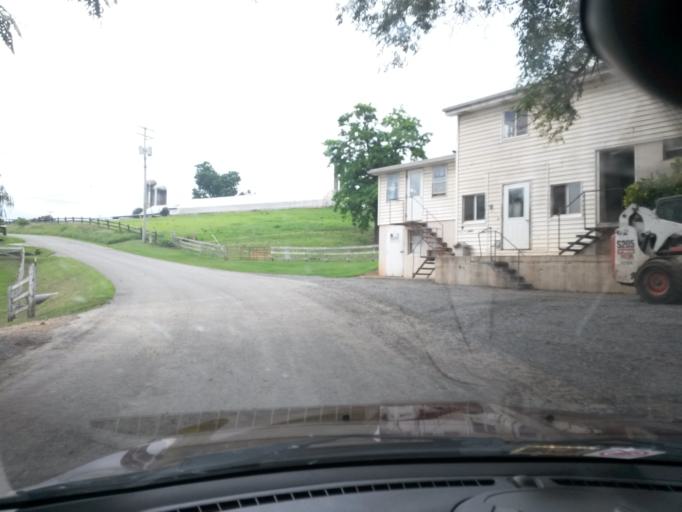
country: US
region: Virginia
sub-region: Rockingham County
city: Dayton
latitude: 38.4426
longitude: -78.9517
